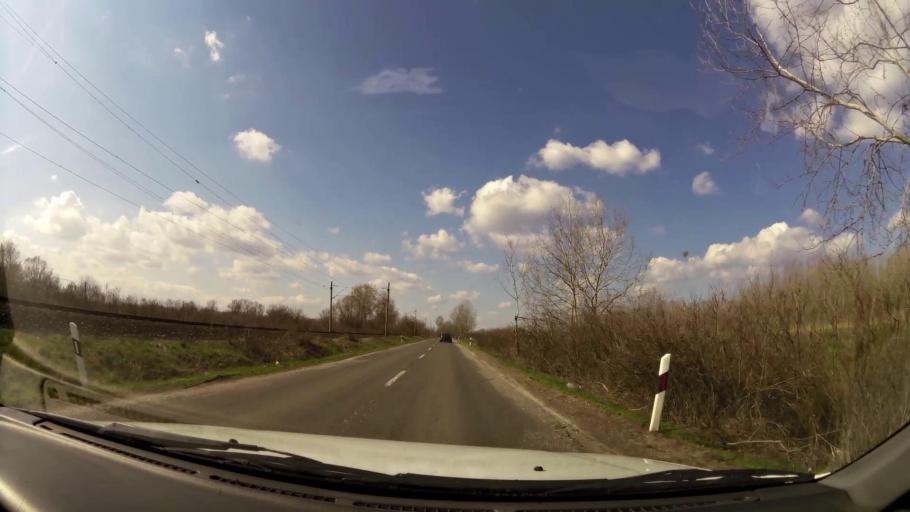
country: HU
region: Pest
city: Nagykata
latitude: 47.3796
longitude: 19.7881
